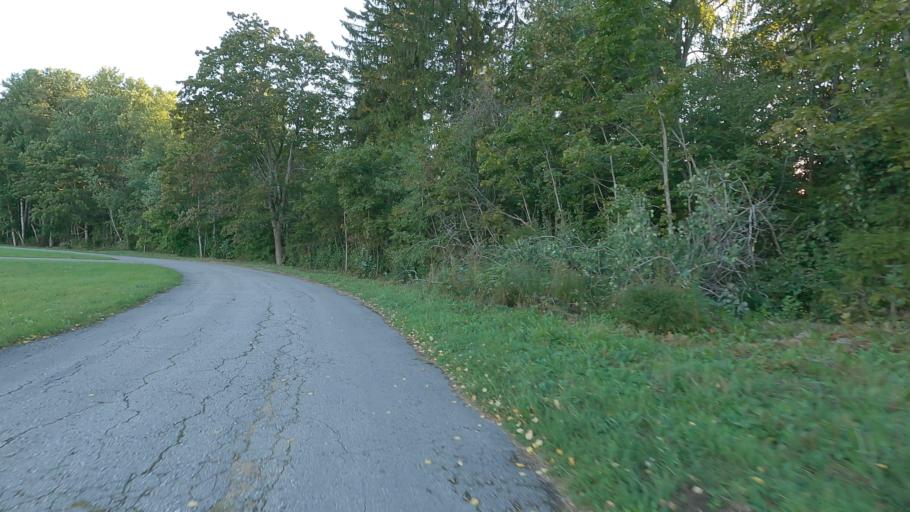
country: EE
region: Raplamaa
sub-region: Rapla vald
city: Rapla
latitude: 58.9995
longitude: 24.7794
